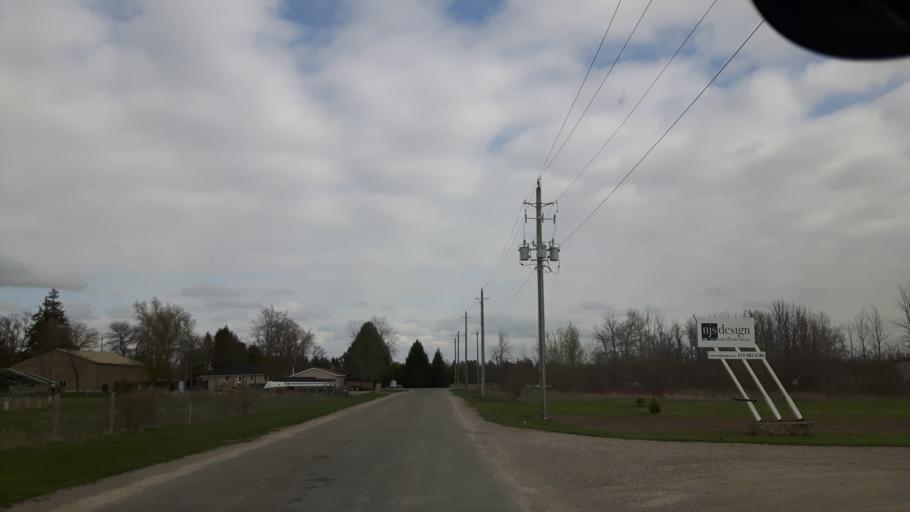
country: CA
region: Ontario
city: Bluewater
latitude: 43.6106
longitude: -81.5445
